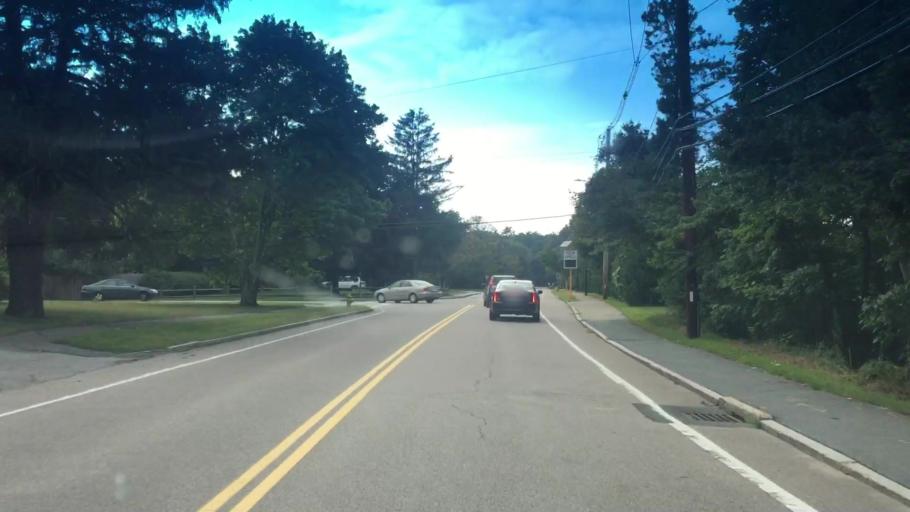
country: US
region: Massachusetts
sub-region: Norfolk County
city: Westwood
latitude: 42.2063
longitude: -71.2324
